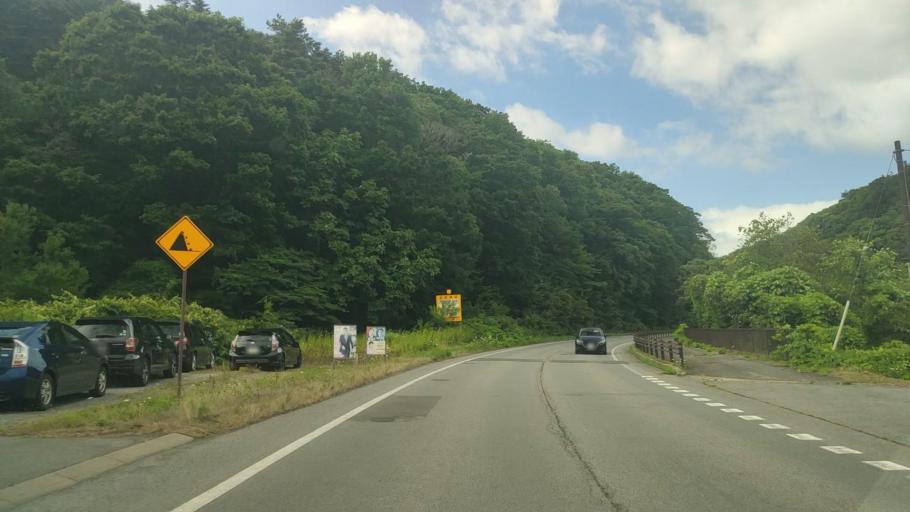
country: JP
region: Hokkaido
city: Date
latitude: 42.5583
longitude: 140.8866
